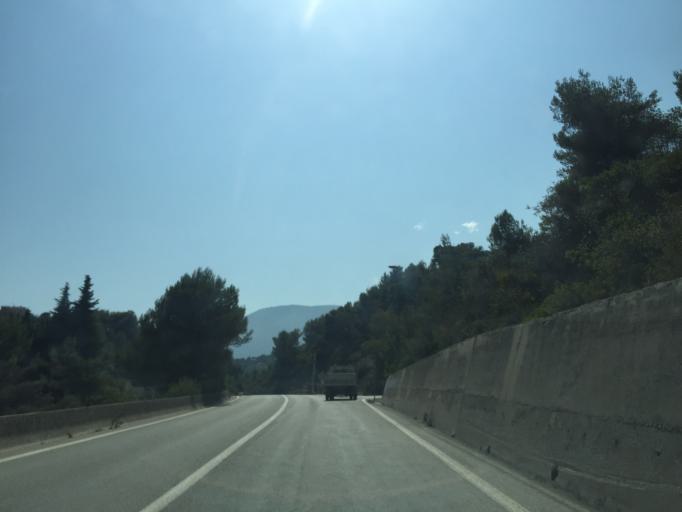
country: FR
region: Provence-Alpes-Cote d'Azur
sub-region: Departement des Alpes-Maritimes
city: Sainte-Agnes
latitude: 43.7985
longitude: 7.4851
